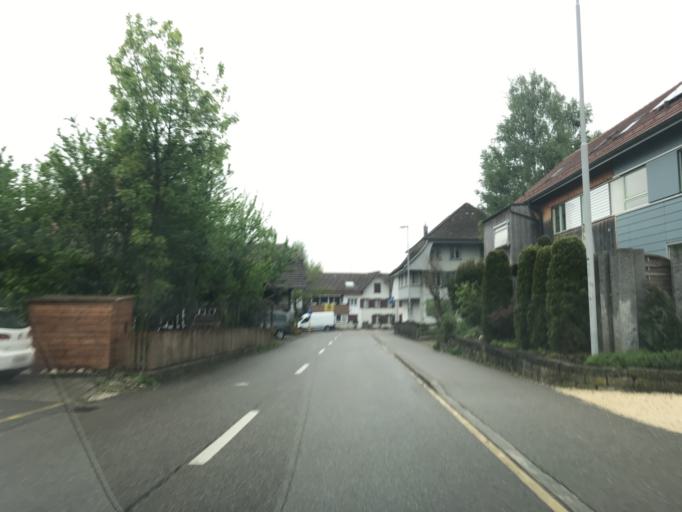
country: CH
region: Bern
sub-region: Oberaargau
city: Langenthal
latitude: 47.2091
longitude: 7.7754
